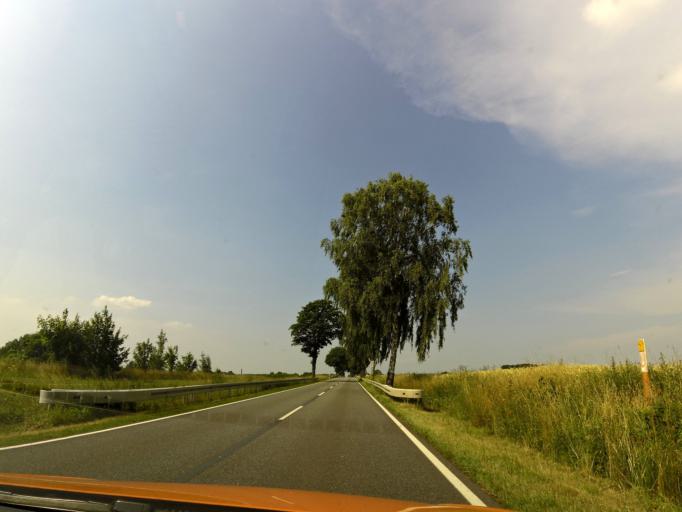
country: DE
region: Mecklenburg-Vorpommern
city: Krakow am See
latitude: 53.7209
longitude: 12.2779
